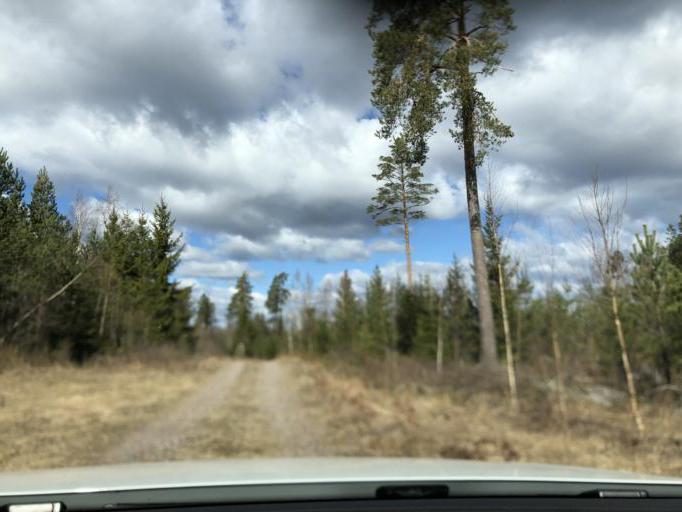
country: SE
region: Uppsala
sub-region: Tierps Kommun
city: Tierp
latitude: 60.3302
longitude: 17.3398
